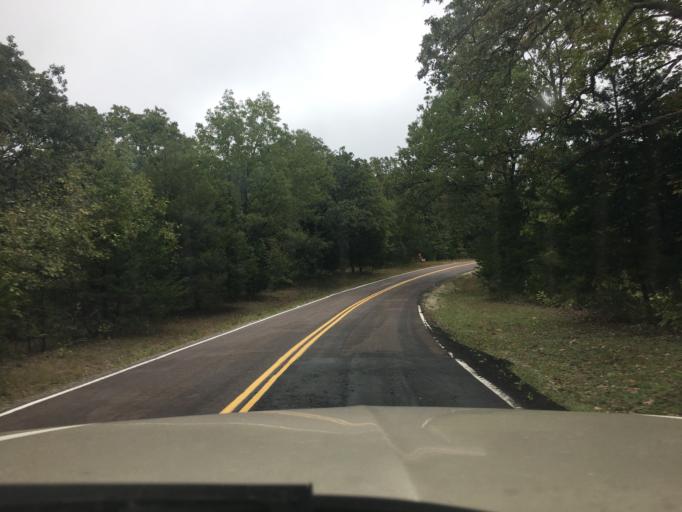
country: US
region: Missouri
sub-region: Crawford County
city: Cuba
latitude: 38.1974
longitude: -91.4589
